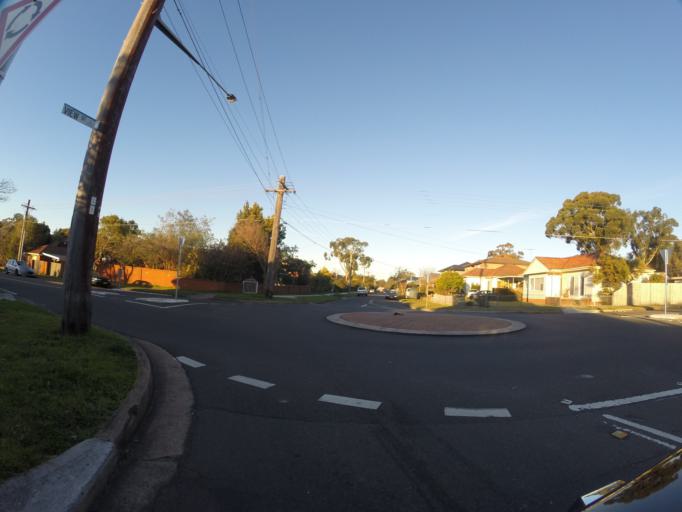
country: AU
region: New South Wales
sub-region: Sutherland Shire
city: Miranda
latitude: -34.0386
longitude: 151.0976
